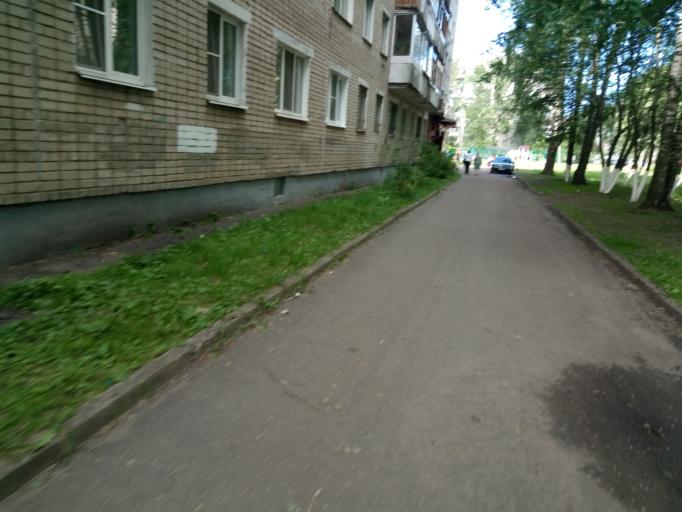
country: RU
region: Jaroslavl
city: Yaroslavl
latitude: 57.6498
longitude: 39.9424
